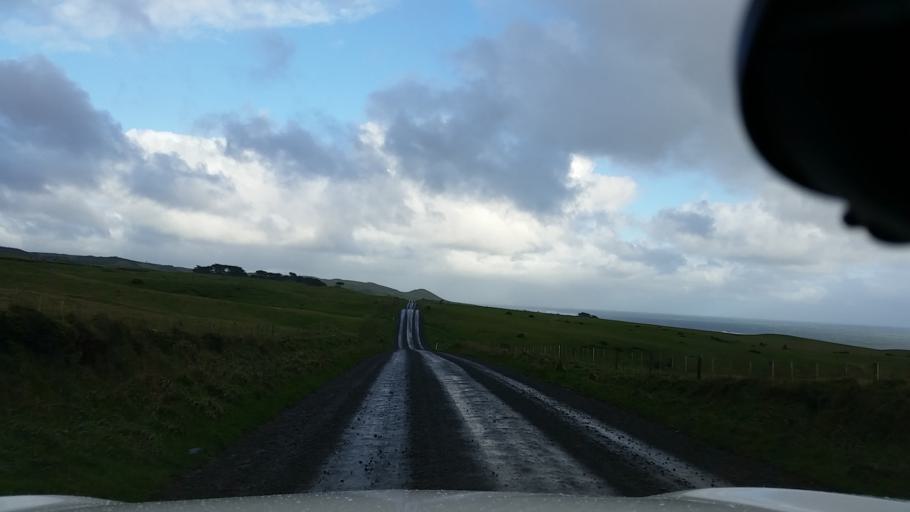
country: NZ
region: Chatham Islands
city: Waitangi
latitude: -43.9876
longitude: -176.6124
